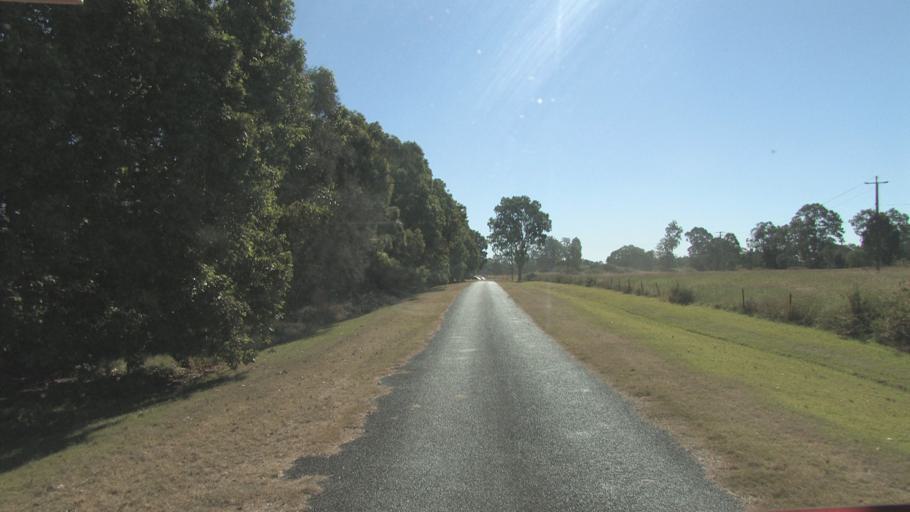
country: AU
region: Queensland
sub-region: Logan
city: Waterford West
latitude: -27.7021
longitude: 153.1290
